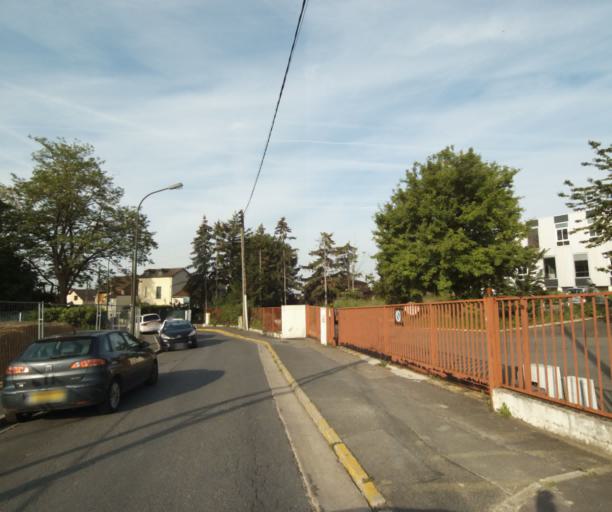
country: FR
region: Ile-de-France
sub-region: Departement du Val-d'Oise
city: Argenteuil
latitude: 48.9568
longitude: 2.2619
